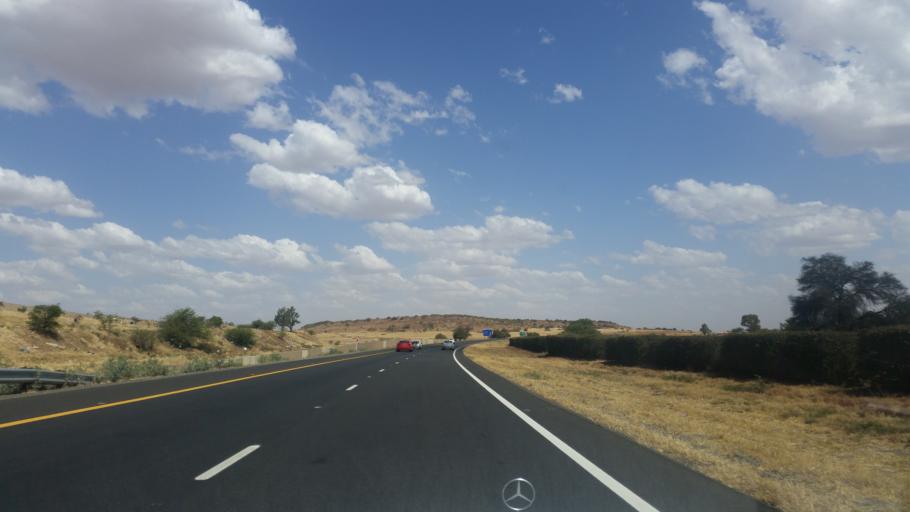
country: ZA
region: Orange Free State
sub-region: Mangaung Metropolitan Municipality
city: Bloemfontein
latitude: -29.1845
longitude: 26.1923
